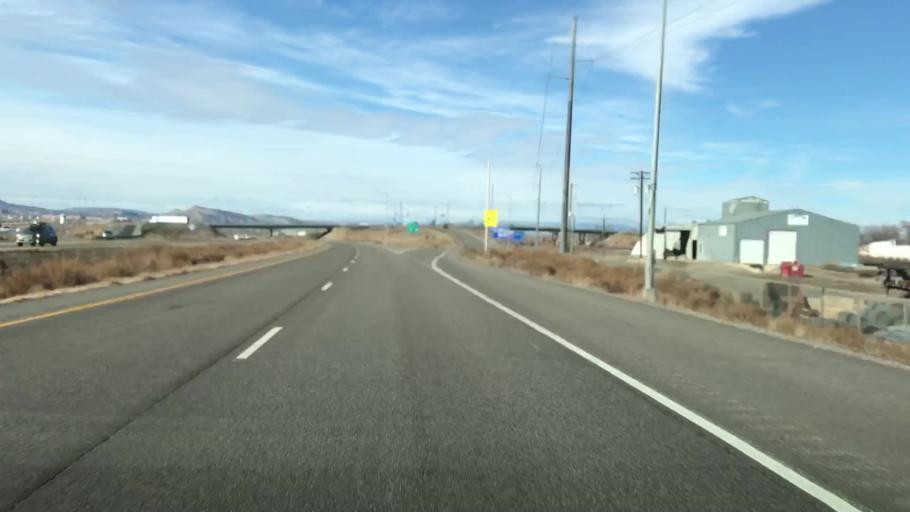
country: US
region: Colorado
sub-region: Mesa County
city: Fruita
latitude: 39.1521
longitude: -108.7323
